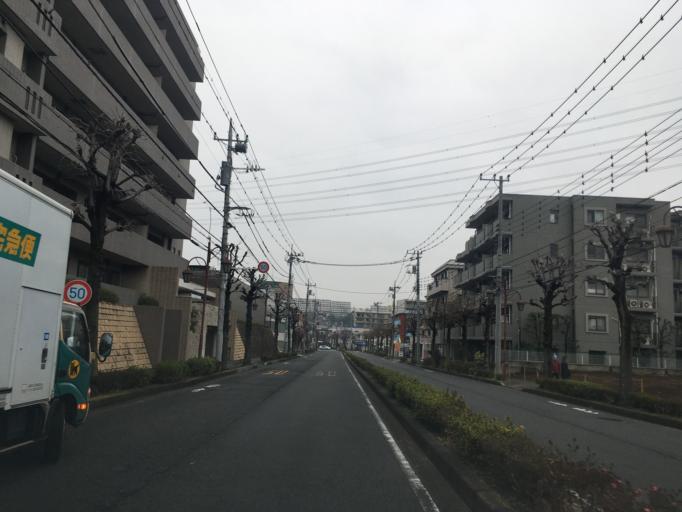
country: JP
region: Tokyo
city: Hino
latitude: 35.6243
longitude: 139.4312
